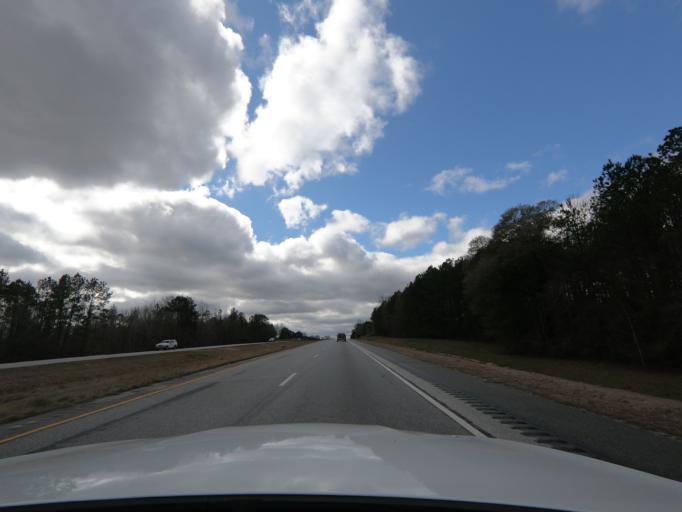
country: US
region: Alabama
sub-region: Russell County
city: Ladonia
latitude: 32.3737
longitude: -85.0903
